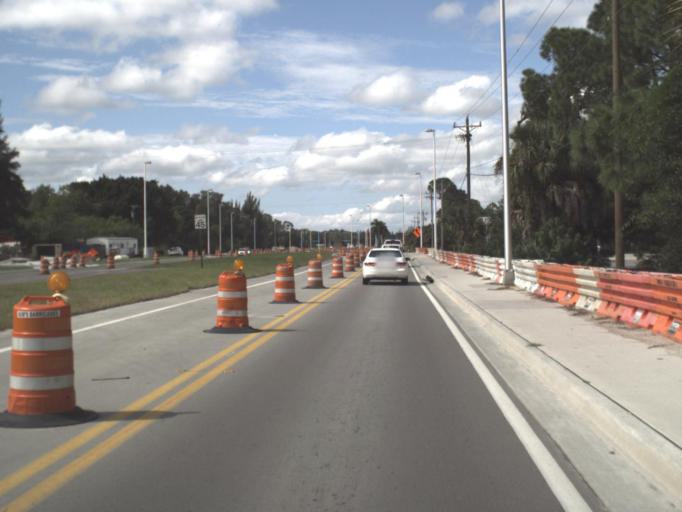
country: US
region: Florida
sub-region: Lee County
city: Palmona Park
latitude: 26.7064
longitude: -81.8965
